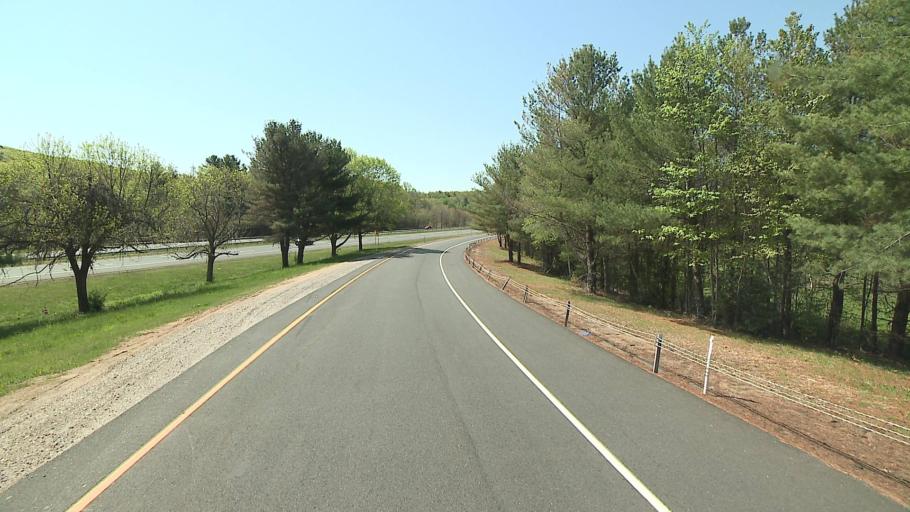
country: US
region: Massachusetts
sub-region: Hampden County
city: Holland
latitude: 41.9757
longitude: -72.1839
